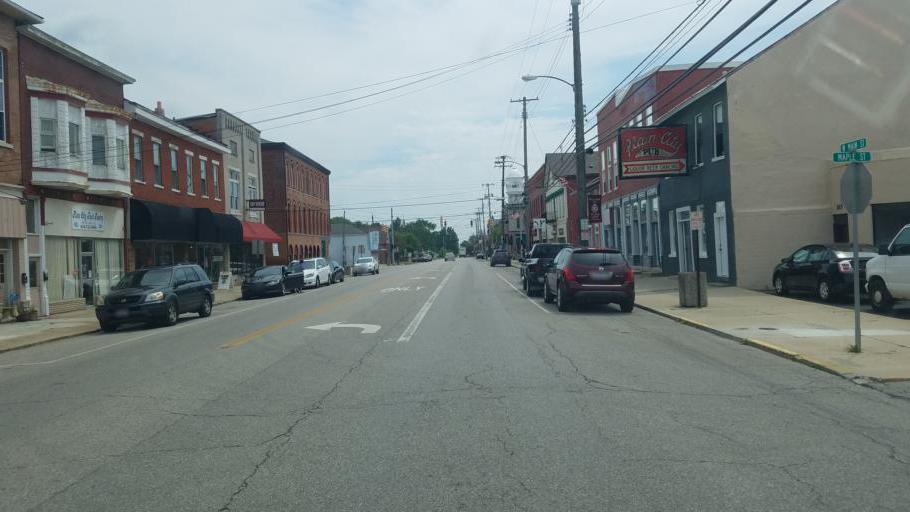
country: US
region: Ohio
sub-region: Madison County
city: Plain City
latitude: 40.1080
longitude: -83.2682
